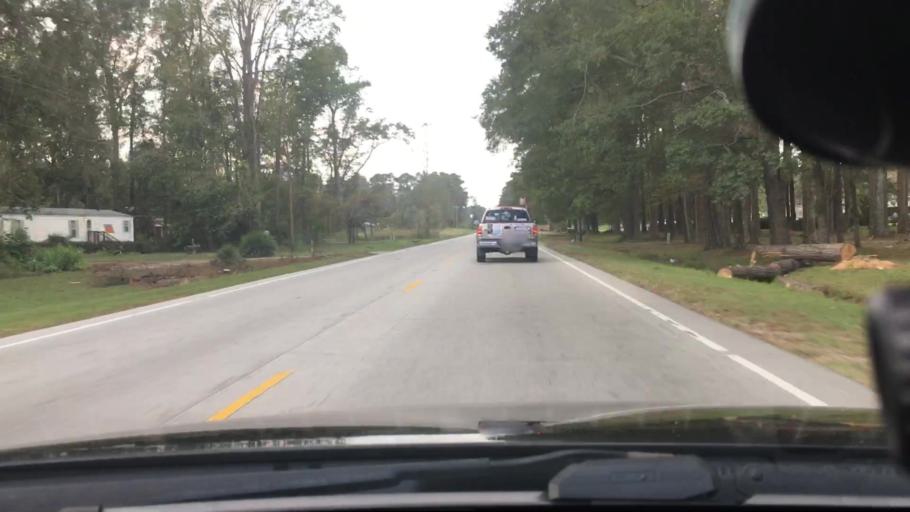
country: US
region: North Carolina
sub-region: Craven County
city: Vanceboro
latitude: 35.2656
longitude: -77.1063
